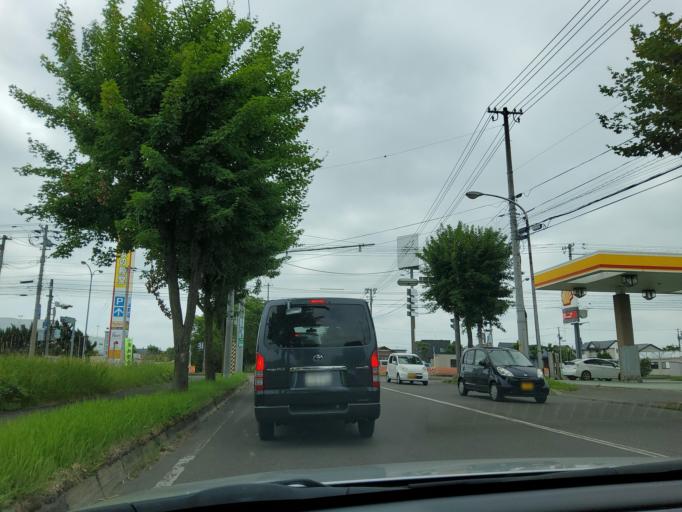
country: JP
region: Hokkaido
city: Obihiro
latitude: 42.9127
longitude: 143.1457
